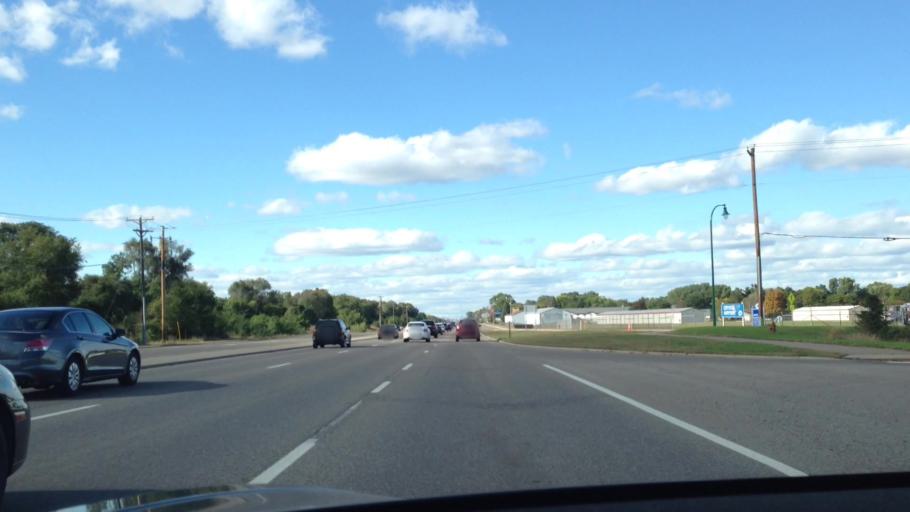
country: US
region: Minnesota
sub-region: Hennepin County
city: Crystal
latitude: 45.0577
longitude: -93.3603
